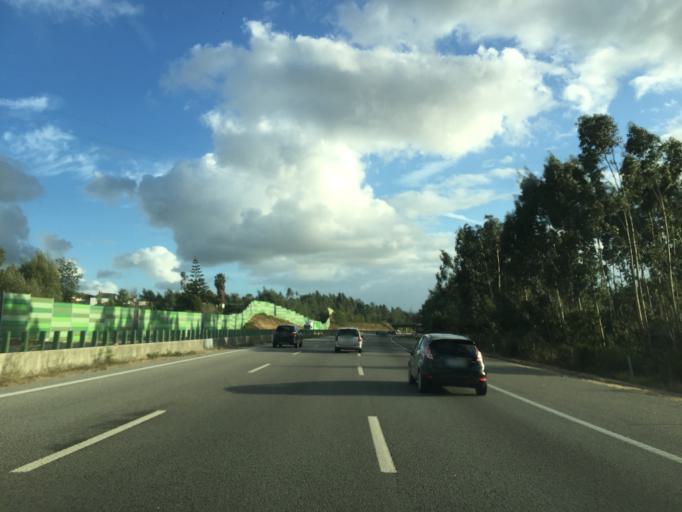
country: PT
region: Coimbra
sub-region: Condeixa-A-Nova
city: Condeixa-a-Nova
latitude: 40.1688
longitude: -8.4937
